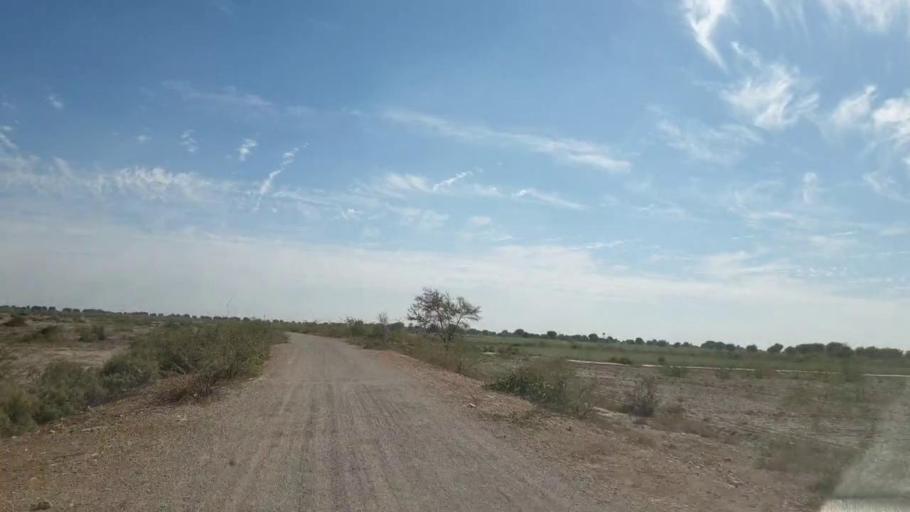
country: PK
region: Sindh
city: Pithoro
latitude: 25.5625
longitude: 69.3020
